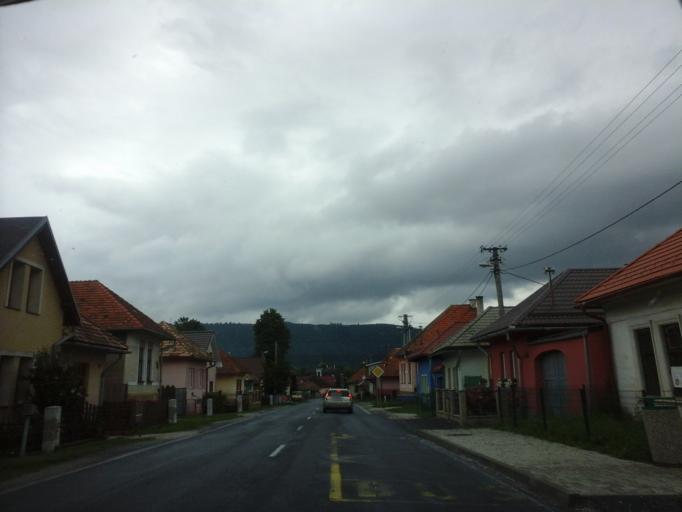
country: SK
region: Presovsky
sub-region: Okres Poprad
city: Poprad
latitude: 48.9835
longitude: 20.3060
